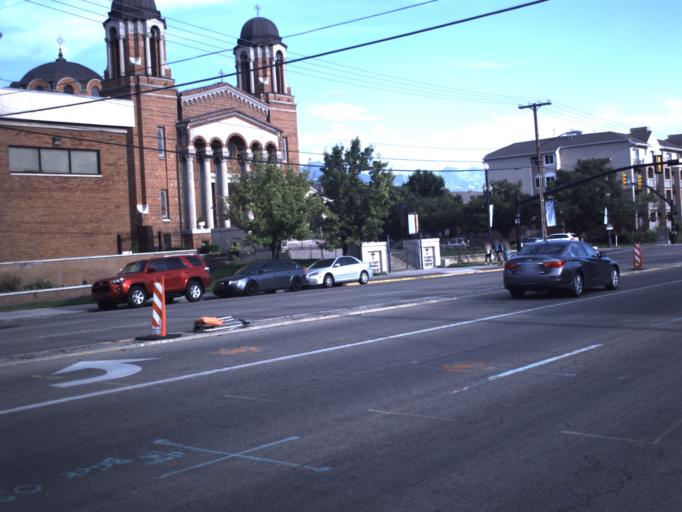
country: US
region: Utah
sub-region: Salt Lake County
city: Salt Lake City
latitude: 40.7636
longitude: -111.8998
